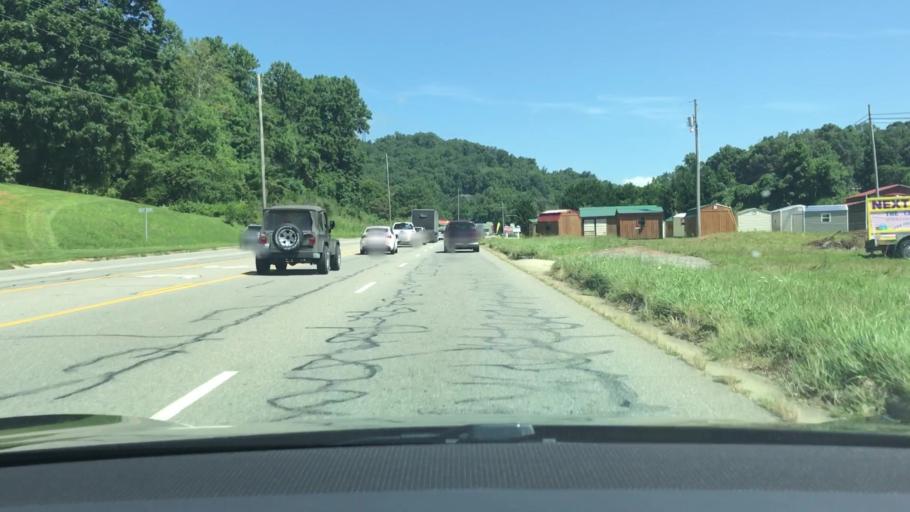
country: US
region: North Carolina
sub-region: Macon County
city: Franklin
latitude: 35.1354
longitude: -83.3976
